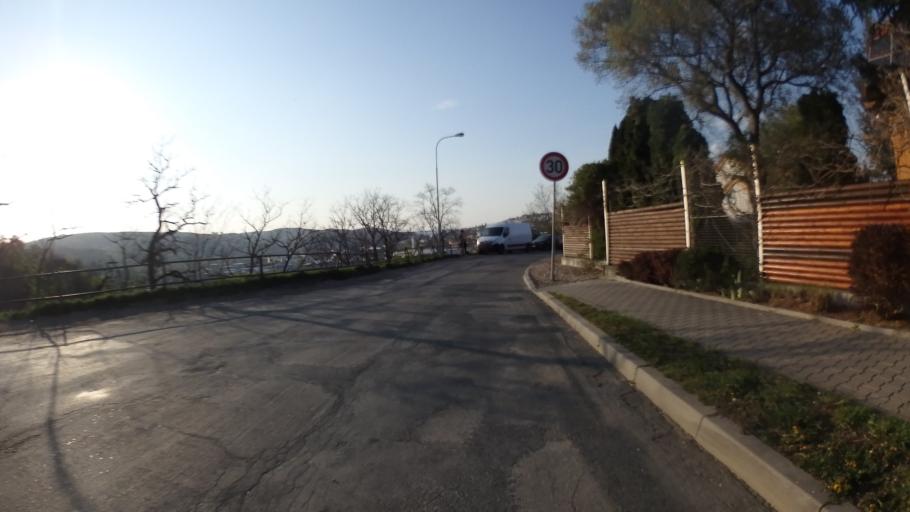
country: CZ
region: South Moravian
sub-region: Mesto Brno
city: Brno
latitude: 49.1827
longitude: 16.5873
